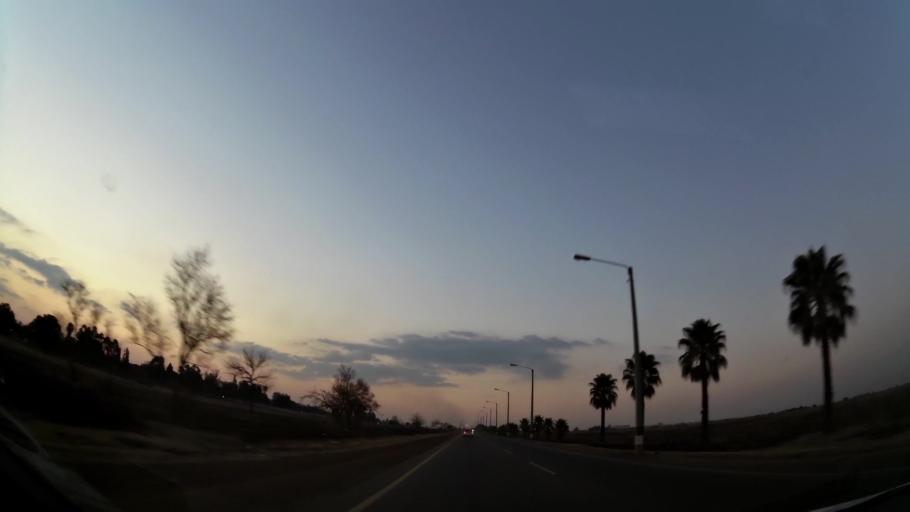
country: ZA
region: Gauteng
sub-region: Ekurhuleni Metropolitan Municipality
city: Springs
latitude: -26.3074
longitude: 28.4551
